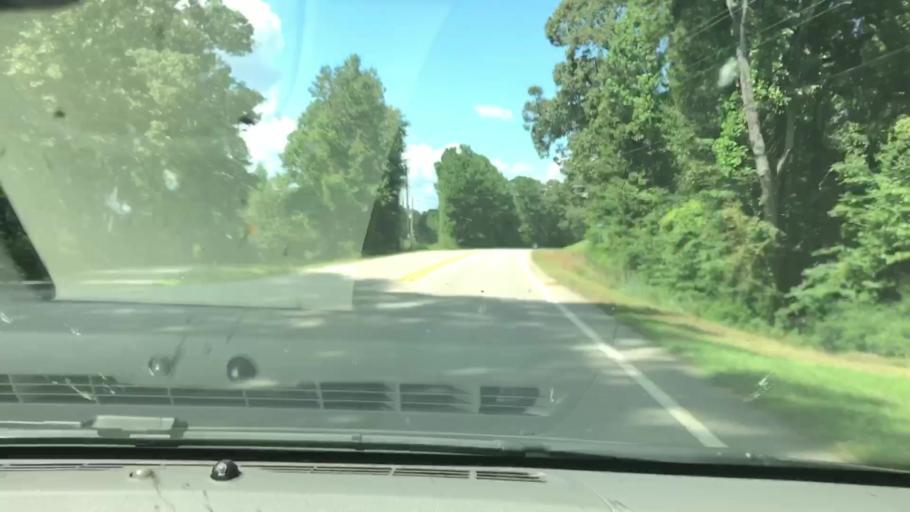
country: US
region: Georgia
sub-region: Troup County
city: La Grange
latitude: 33.1191
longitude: -85.0889
